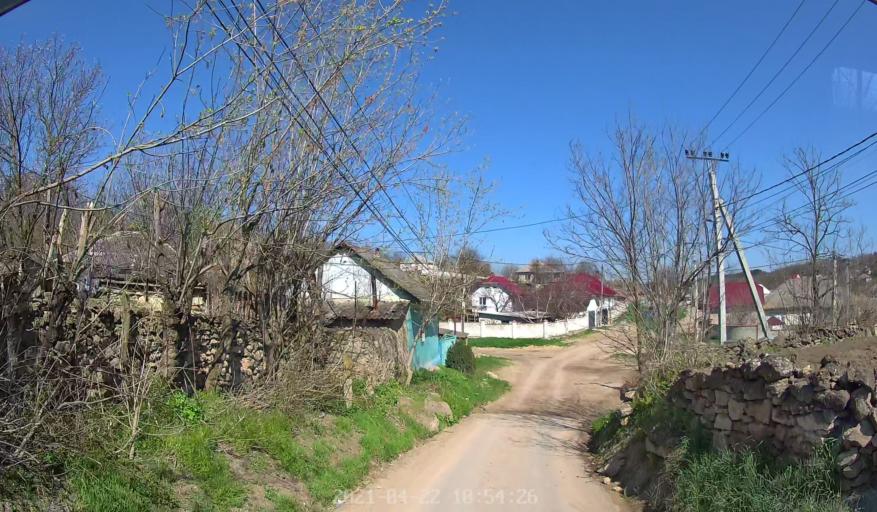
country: MD
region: Chisinau
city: Ciorescu
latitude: 47.1691
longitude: 28.9498
